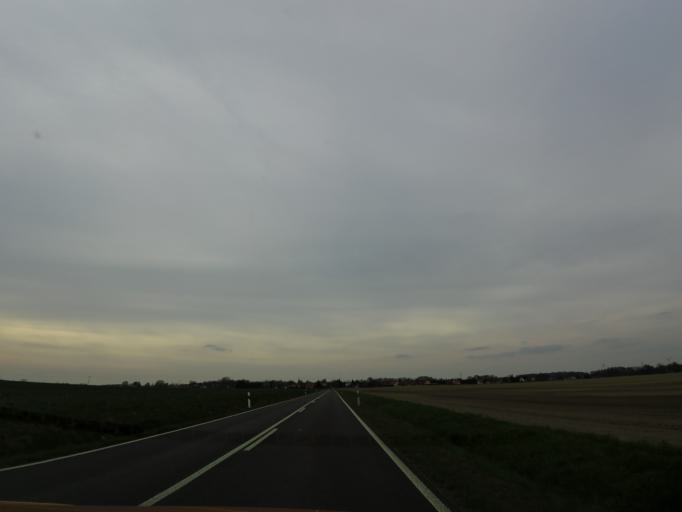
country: DE
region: Brandenburg
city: Tauche
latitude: 52.1796
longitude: 14.1732
